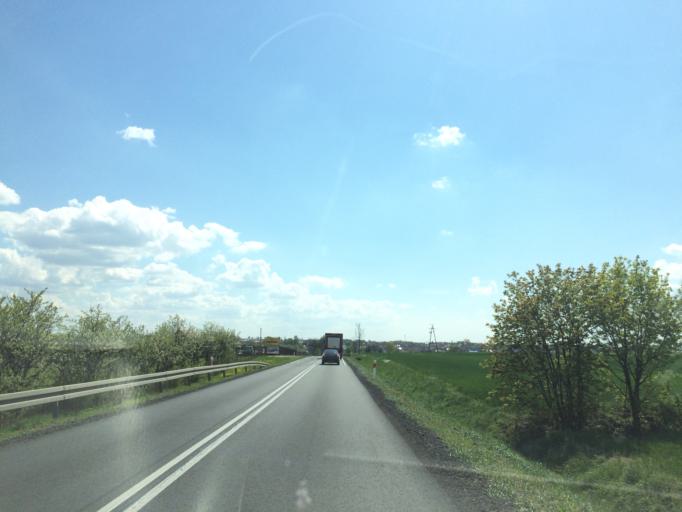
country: PL
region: Warmian-Masurian Voivodeship
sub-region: Powiat ilawski
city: Lubawa
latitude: 53.5209
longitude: 19.7466
